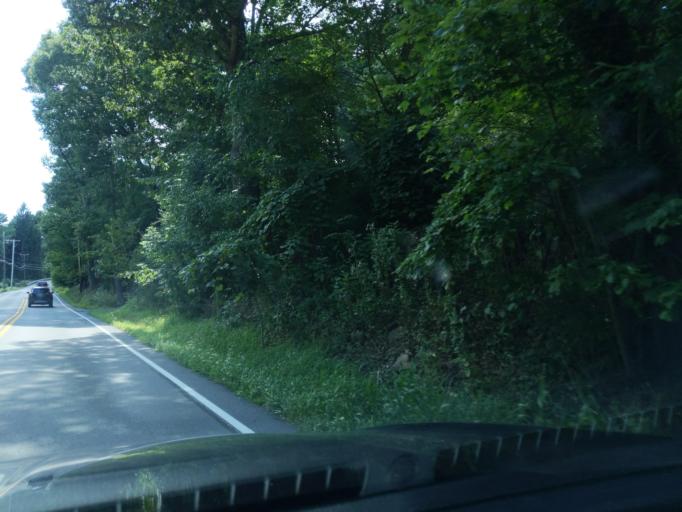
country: US
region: Pennsylvania
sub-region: Blair County
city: Greenwood
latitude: 40.5151
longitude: -78.3212
